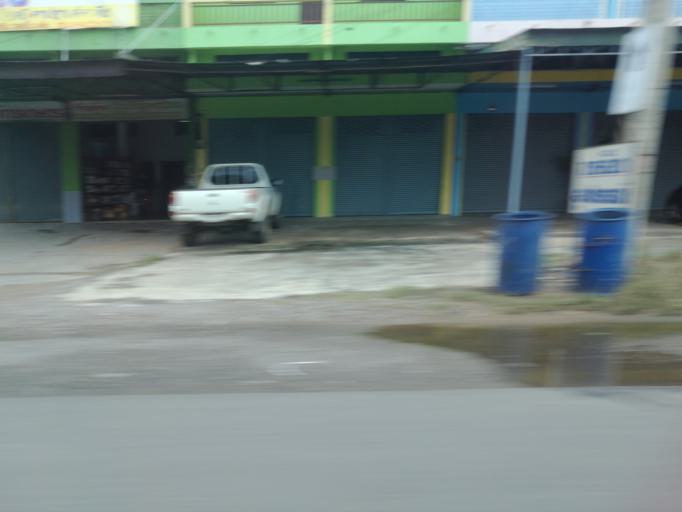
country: TH
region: Prachuap Khiri Khan
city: Pran Buri
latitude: 12.3560
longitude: 99.8840
